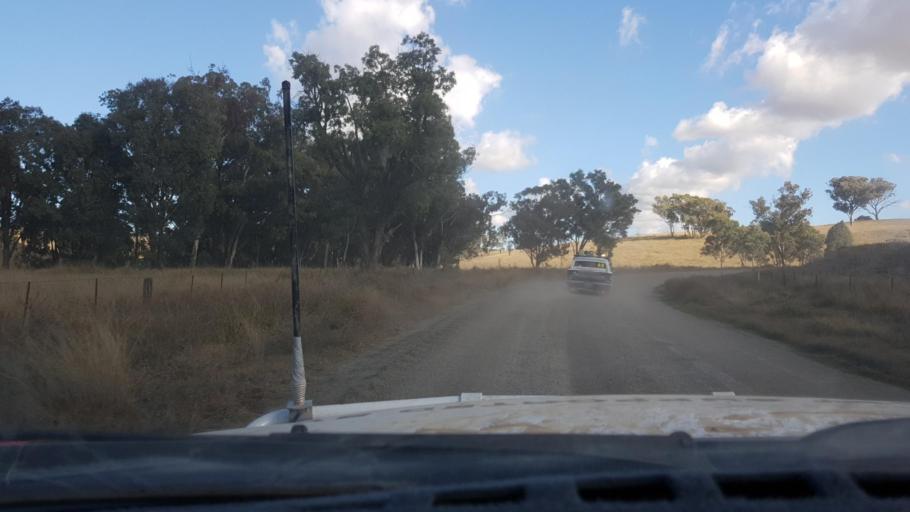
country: AU
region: New South Wales
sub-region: Tamworth Municipality
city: Manilla
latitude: -30.6131
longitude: 150.5112
